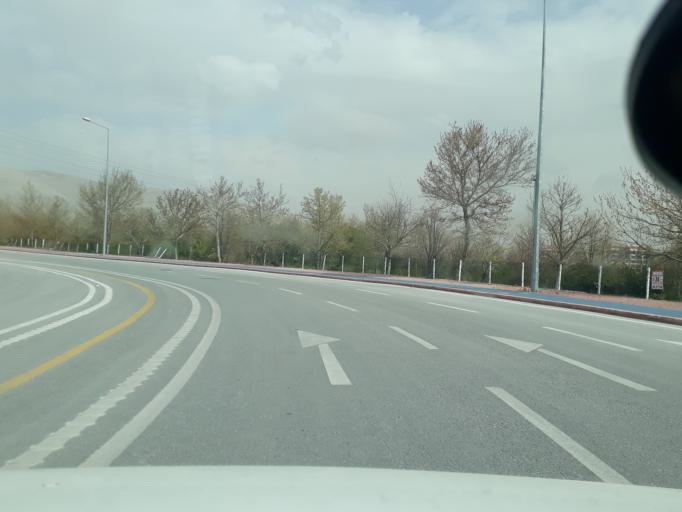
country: TR
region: Konya
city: Selcuklu
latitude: 37.9461
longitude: 32.4804
